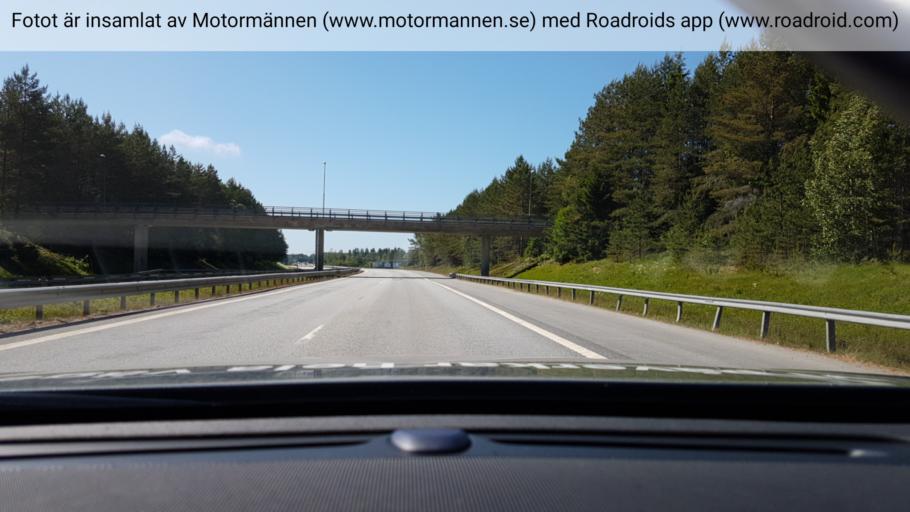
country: SE
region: Vaesterbotten
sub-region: Umea Kommun
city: Roback
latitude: 63.7821
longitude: 20.1949
